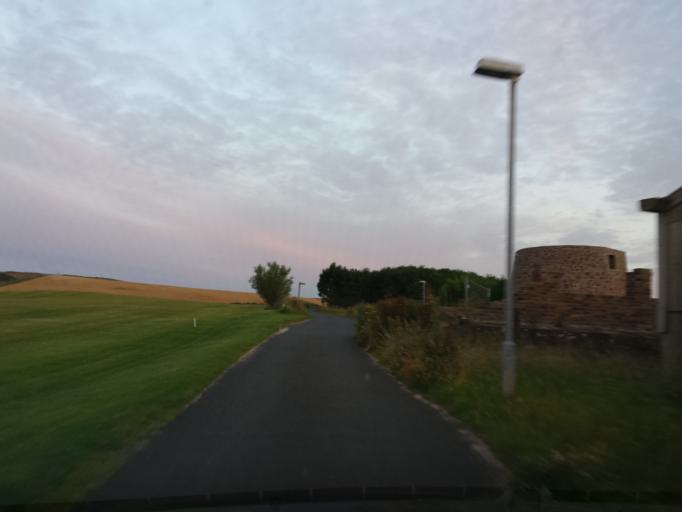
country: GB
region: Scotland
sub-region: The Scottish Borders
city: Eyemouth
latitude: 55.8670
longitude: -2.0851
